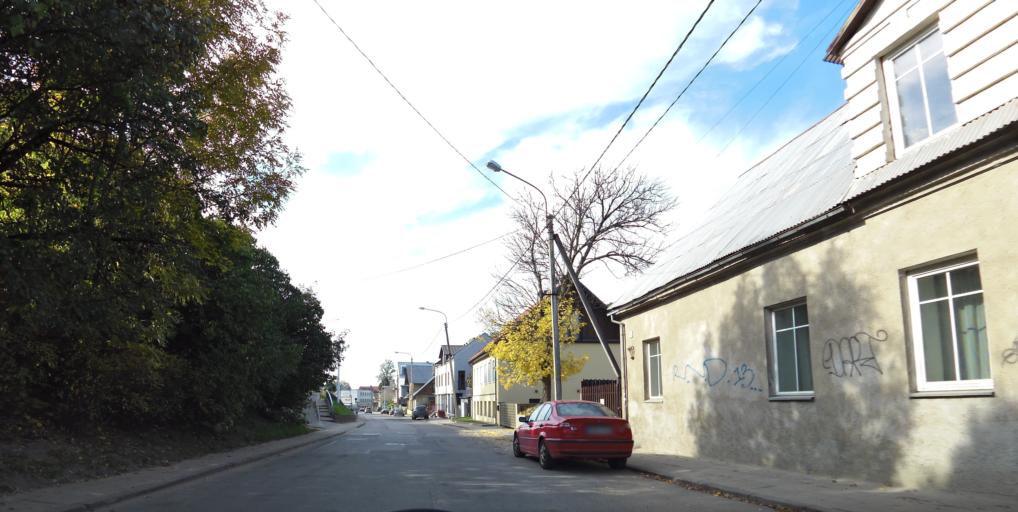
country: LT
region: Vilnius County
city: Rasos
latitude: 54.6822
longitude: 25.3085
